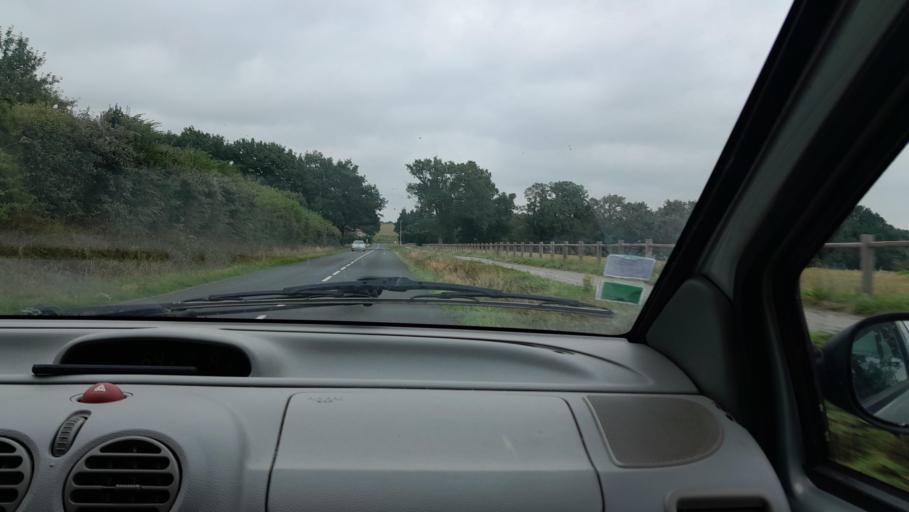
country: FR
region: Pays de la Loire
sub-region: Departement de la Mayenne
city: Cosse-le-Vivien
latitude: 47.9380
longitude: -0.9006
